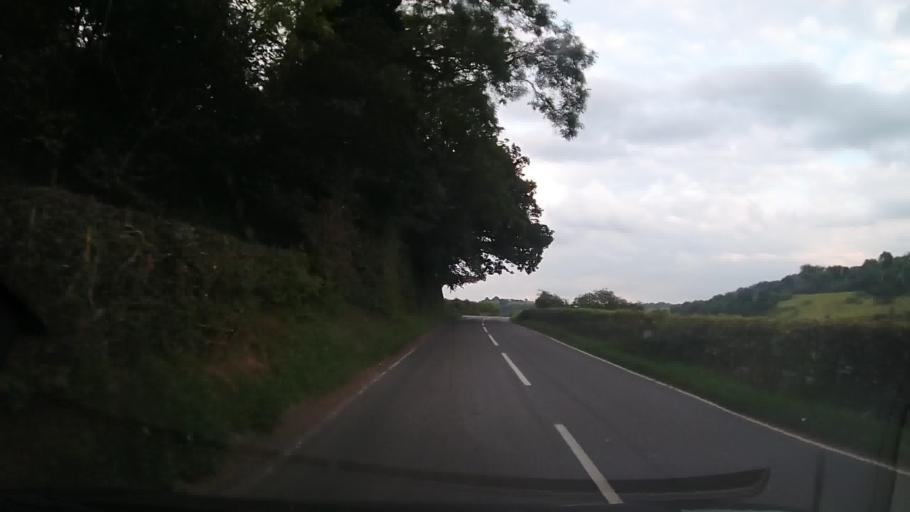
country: GB
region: Wales
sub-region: Sir Powys
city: Llanfechain
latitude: 52.8067
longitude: -3.1849
